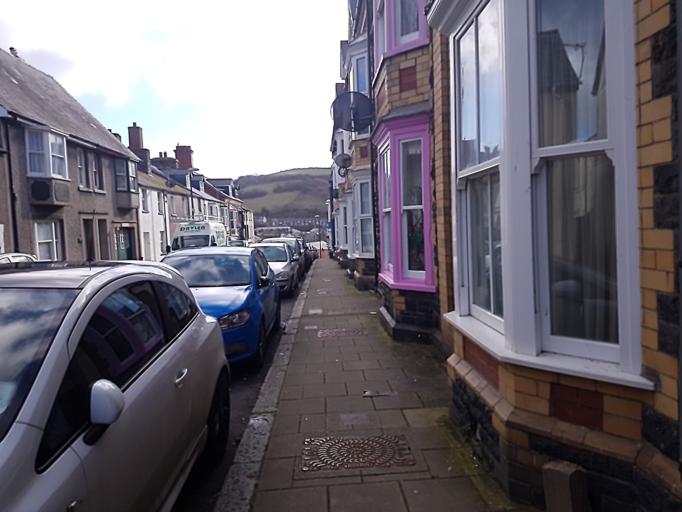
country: GB
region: Wales
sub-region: County of Ceredigion
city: Aberystwyth
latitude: 52.4131
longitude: -4.0866
